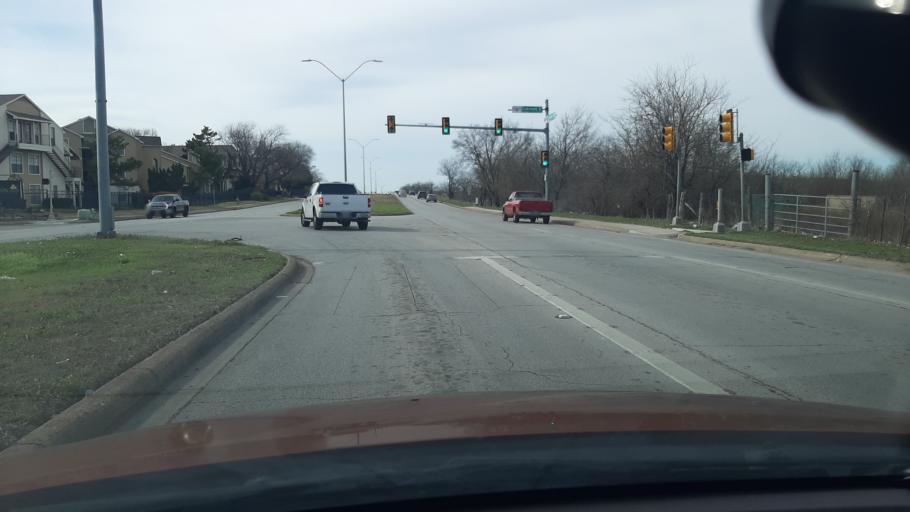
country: US
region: Texas
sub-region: Tarrant County
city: Benbrook
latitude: 32.6630
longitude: -97.4078
